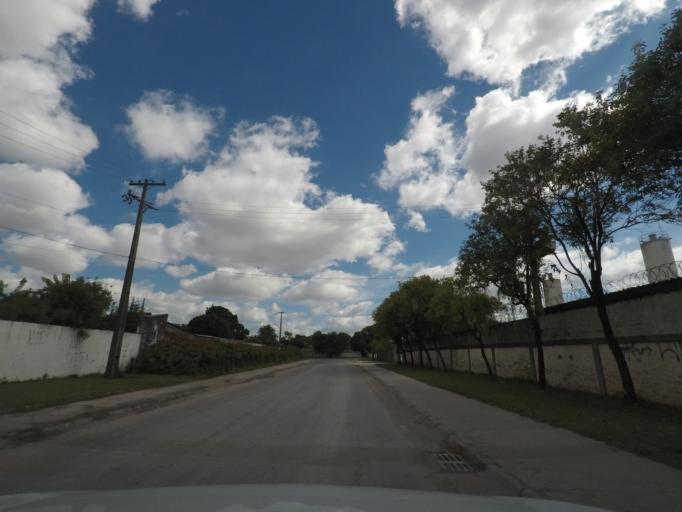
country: BR
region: Parana
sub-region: Sao Jose Dos Pinhais
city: Sao Jose dos Pinhais
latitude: -25.4949
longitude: -49.2305
